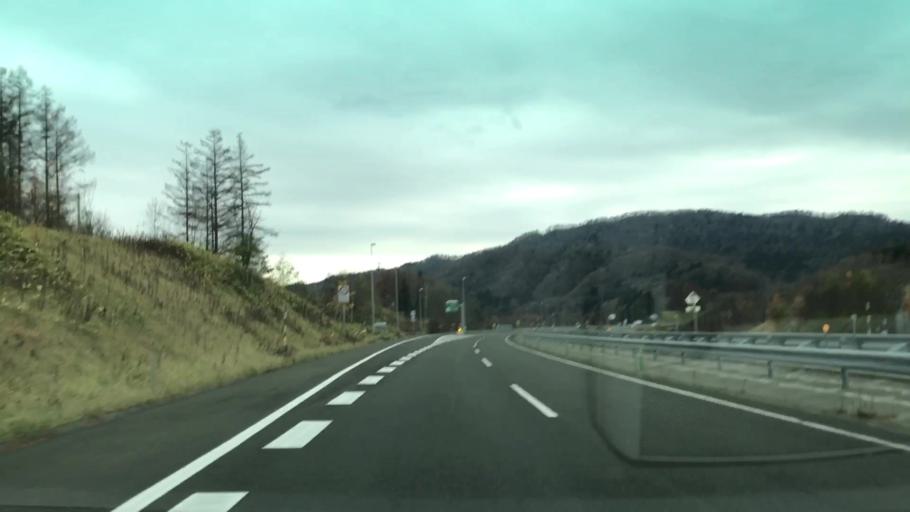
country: JP
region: Hokkaido
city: Shimo-furano
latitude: 42.9207
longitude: 142.1990
